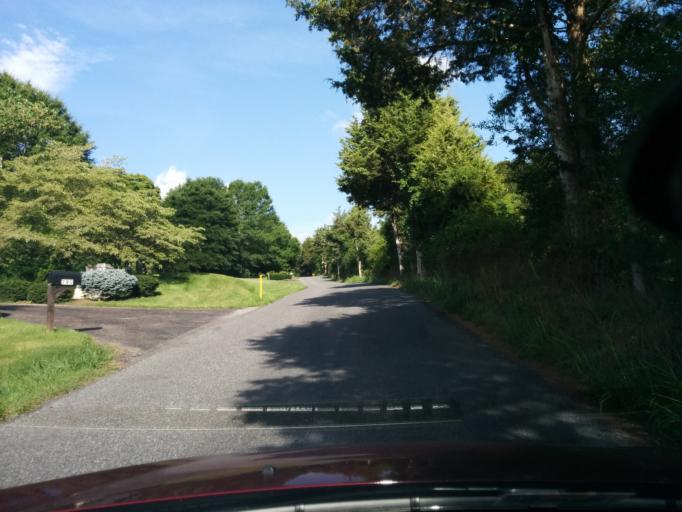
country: US
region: Virginia
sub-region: City of Lexington
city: Lexington
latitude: 37.7783
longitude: -79.4598
